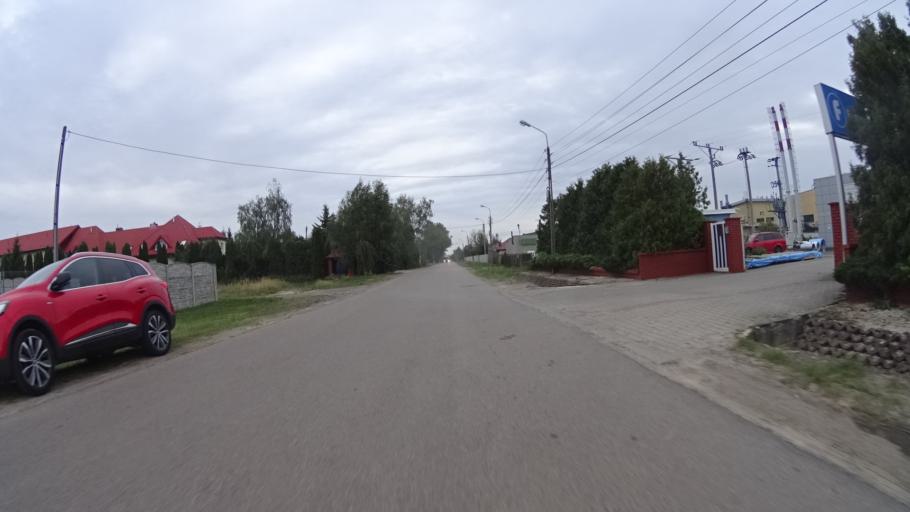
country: PL
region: Masovian Voivodeship
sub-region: Powiat warszawski zachodni
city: Ozarow Mazowiecki
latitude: 52.2475
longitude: 20.7877
